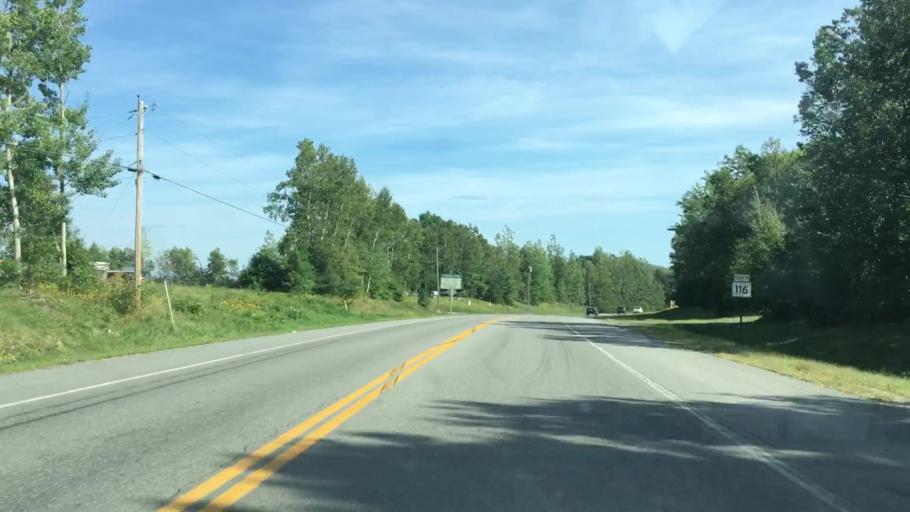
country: US
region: Maine
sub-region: Penobscot County
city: Lincoln
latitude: 45.3698
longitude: -68.5569
